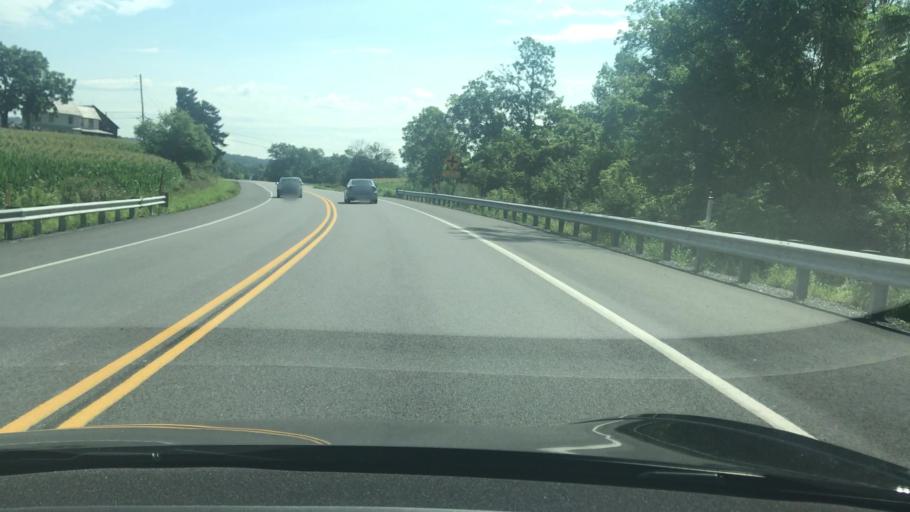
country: US
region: Pennsylvania
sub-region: York County
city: Valley Green
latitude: 40.1289
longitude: -76.8544
